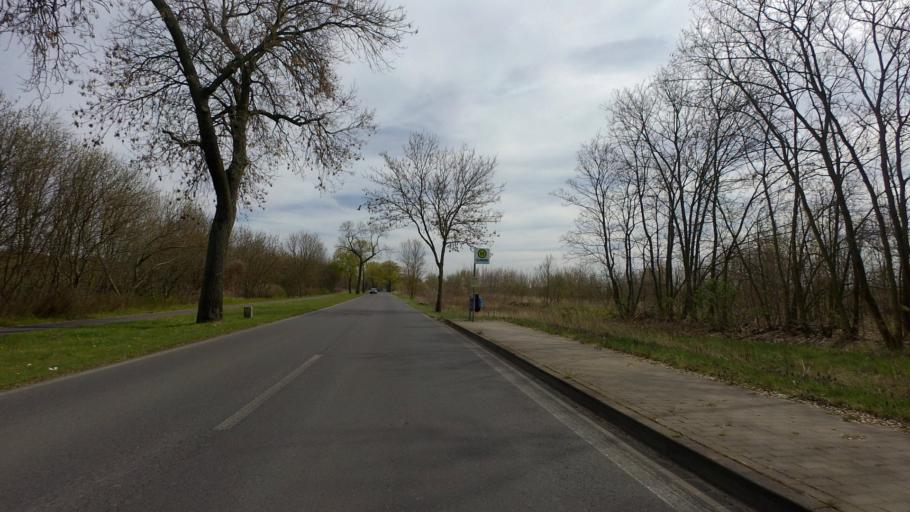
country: DE
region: Berlin
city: Gropiusstadt
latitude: 52.3756
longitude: 13.4548
